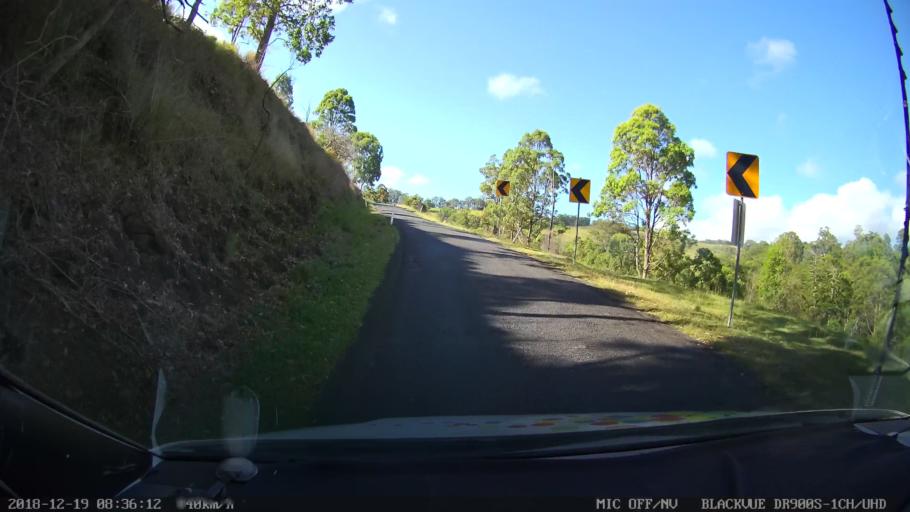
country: AU
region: New South Wales
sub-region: Kyogle
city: Kyogle
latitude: -28.3247
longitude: 152.9728
